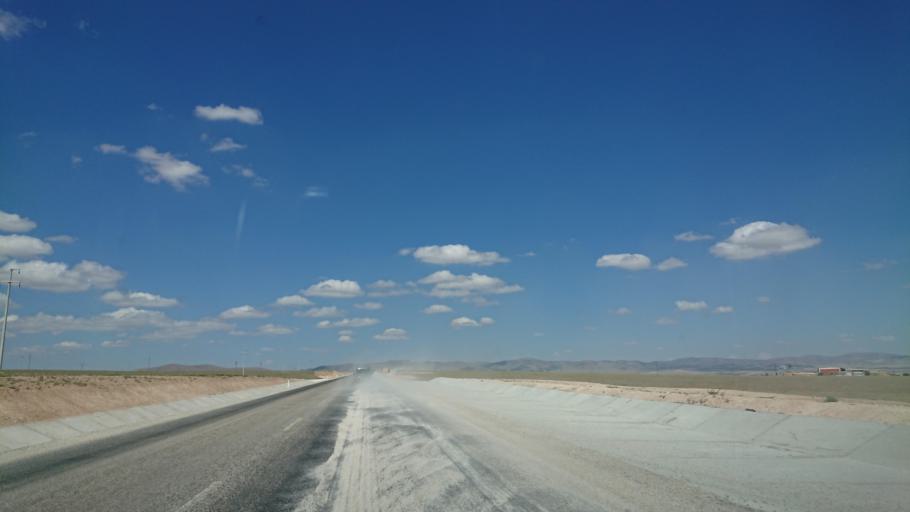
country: TR
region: Kirsehir
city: Kirsehir
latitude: 39.1285
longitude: 34.0365
